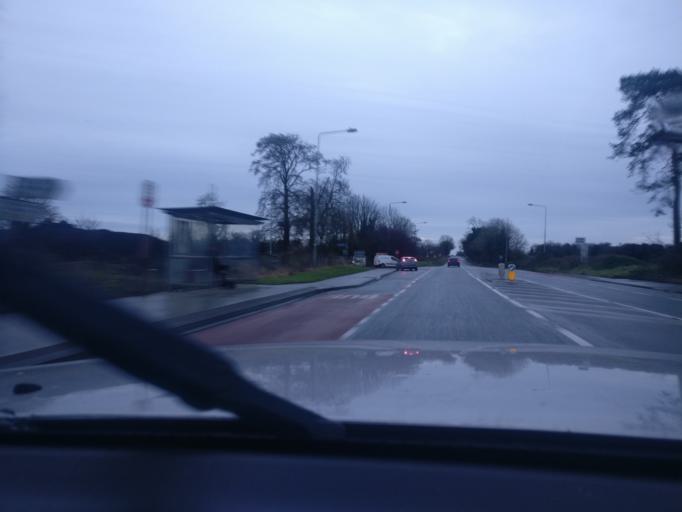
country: IE
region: Leinster
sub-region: An Mhi
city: Navan
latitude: 53.6865
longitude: -6.7685
